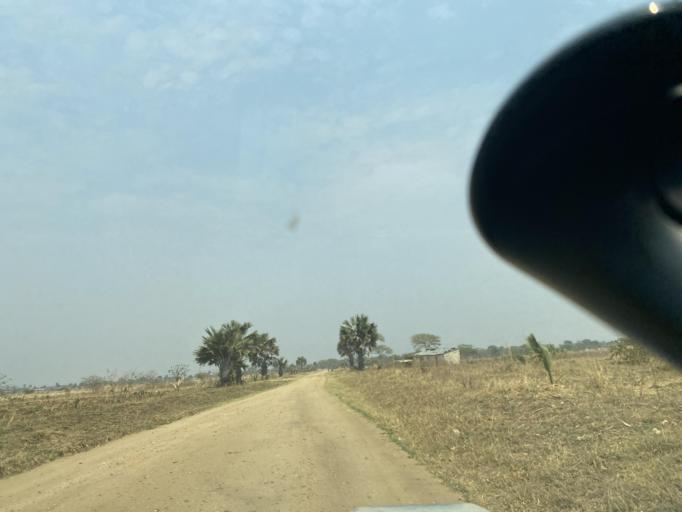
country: ZM
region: Lusaka
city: Kafue
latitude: -15.6483
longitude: 28.0450
